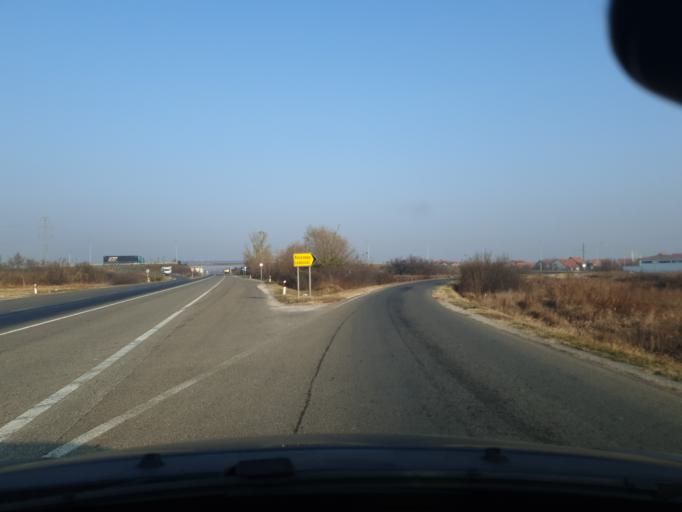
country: RS
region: Central Serbia
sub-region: Jablanicki Okrug
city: Leskovac
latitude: 43.0039
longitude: 21.9659
